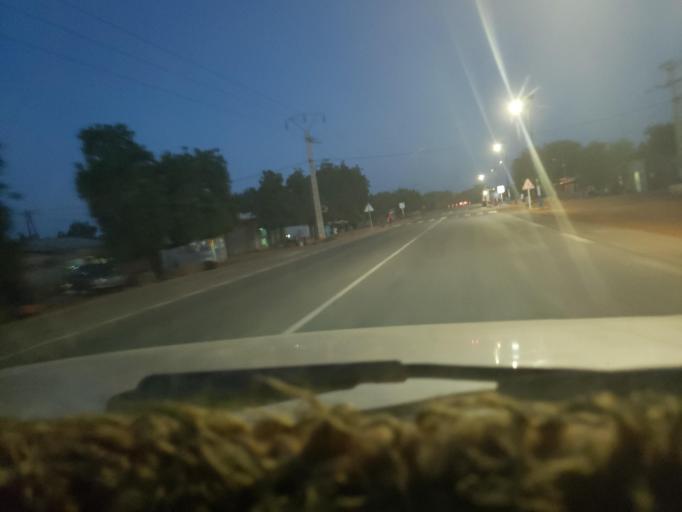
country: SN
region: Louga
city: Ndibene Dahra
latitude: 15.3845
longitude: -15.2373
